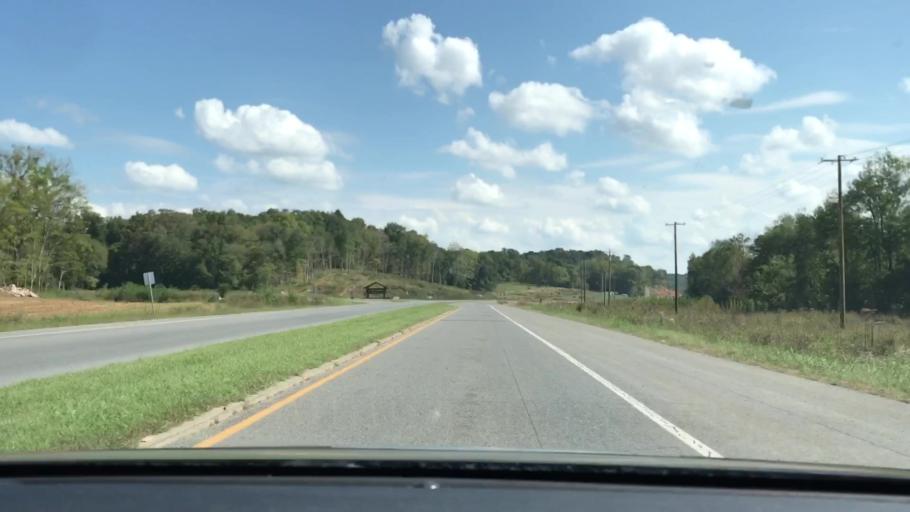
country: US
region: Kentucky
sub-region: Trigg County
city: Cadiz
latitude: 36.8050
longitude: -87.9298
